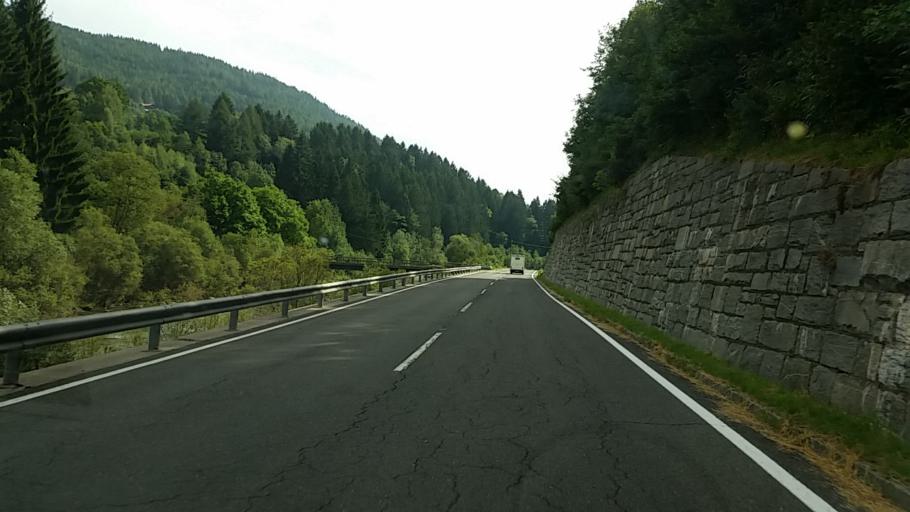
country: AT
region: Carinthia
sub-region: Politischer Bezirk Spittal an der Drau
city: Gmuend
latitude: 46.8936
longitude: 13.5253
